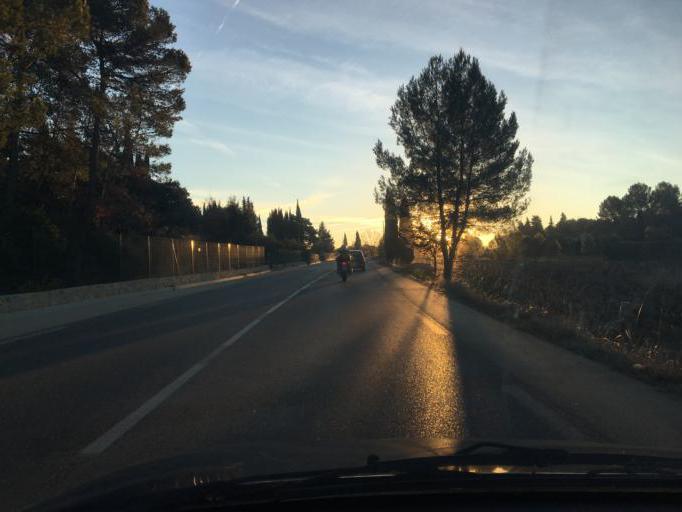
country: FR
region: Provence-Alpes-Cote d'Azur
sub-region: Departement du Var
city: Taradeau
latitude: 43.4659
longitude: 6.3927
